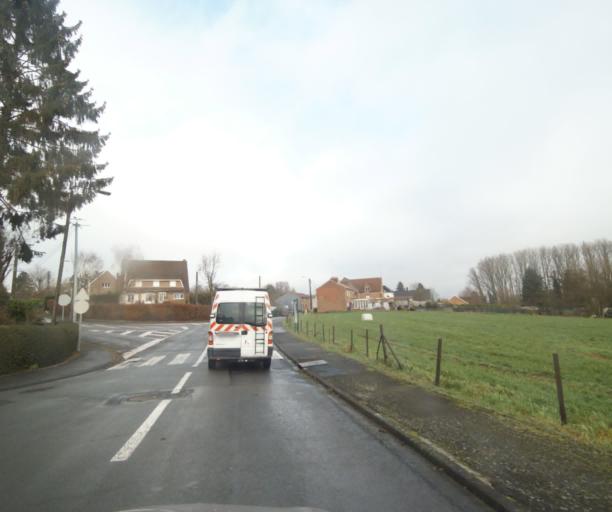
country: FR
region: Nord-Pas-de-Calais
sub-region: Departement du Nord
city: Aulnoy-lez-Valenciennes
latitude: 50.3259
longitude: 3.5267
